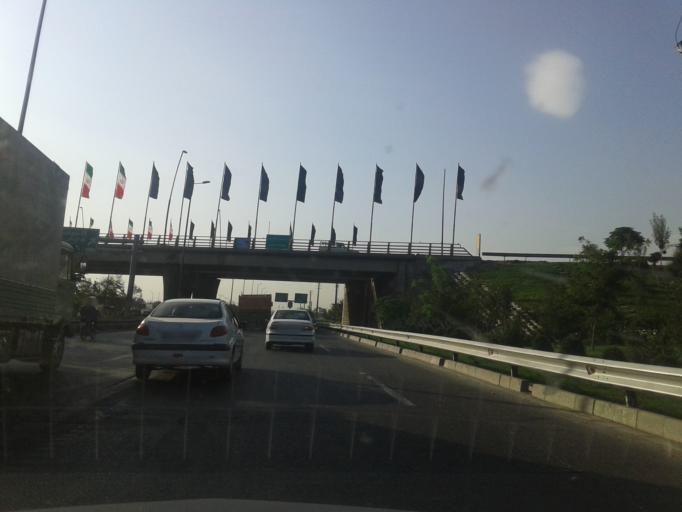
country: IR
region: Tehran
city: Eslamshahr
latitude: 35.6501
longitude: 51.2749
